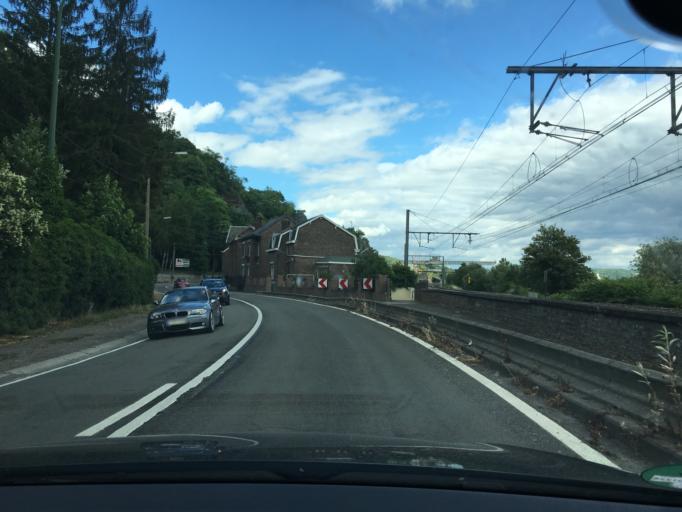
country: BE
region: Wallonia
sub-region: Province de Liege
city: Amay
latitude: 50.5590
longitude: 5.3389
